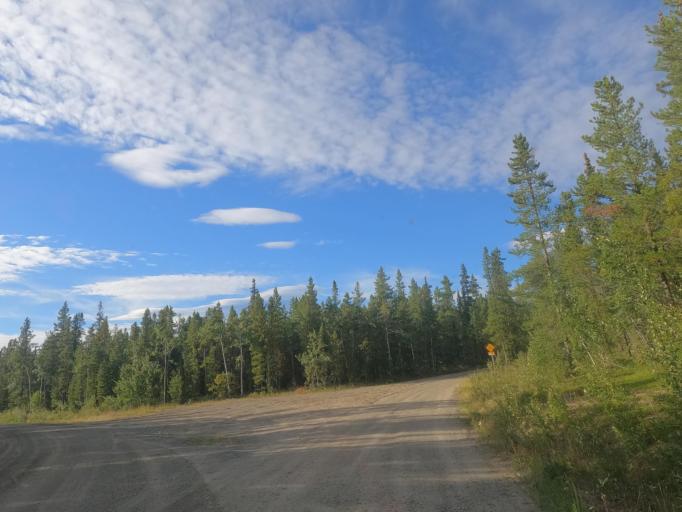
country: CA
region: Yukon
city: Whitehorse
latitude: 60.7581
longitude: -135.0374
